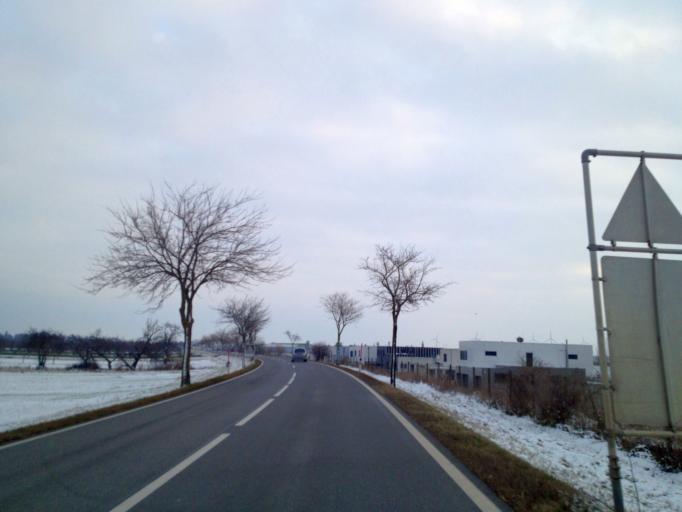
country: AT
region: Lower Austria
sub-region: Politischer Bezirk Bruck an der Leitha
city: Berg
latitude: 48.1015
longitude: 17.0450
